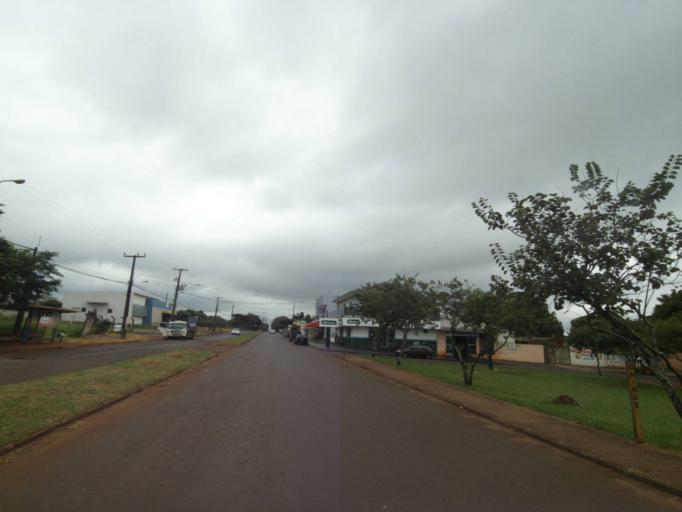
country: BR
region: Parana
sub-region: Campo Mourao
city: Campo Mourao
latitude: -24.0202
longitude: -52.3556
